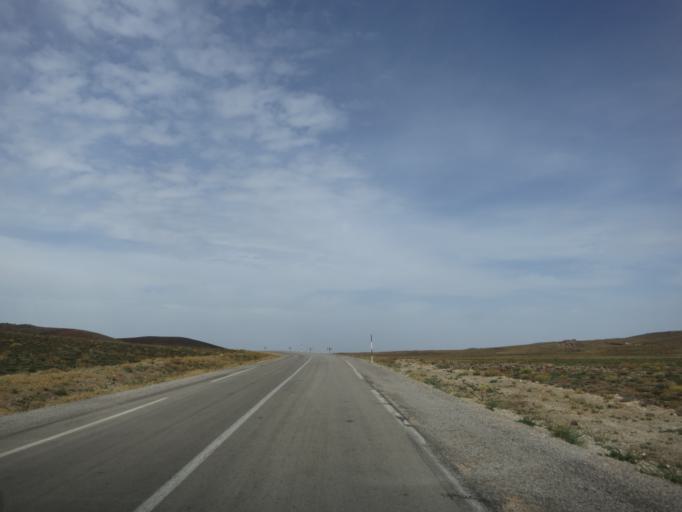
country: MA
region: Meknes-Tafilalet
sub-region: Ifrane
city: Azrou
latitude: 33.3678
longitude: -5.1422
